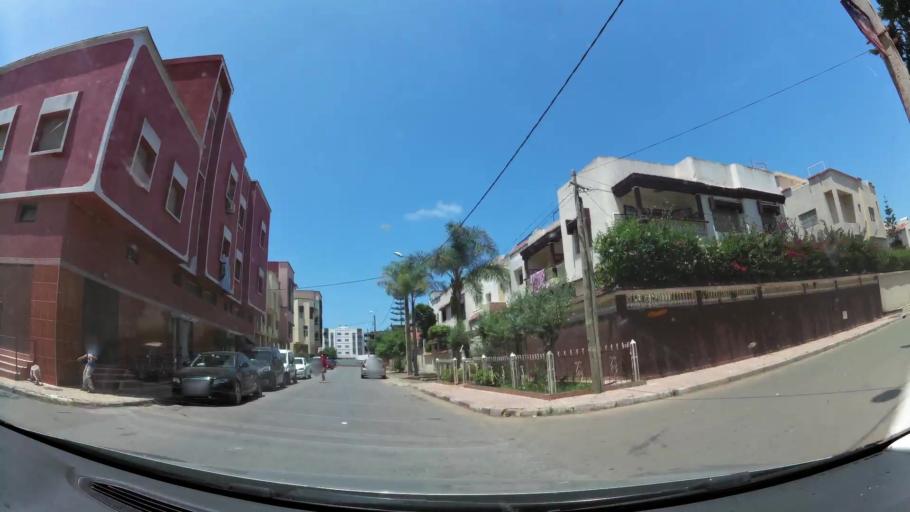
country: MA
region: Gharb-Chrarda-Beni Hssen
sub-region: Kenitra Province
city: Kenitra
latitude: 34.2635
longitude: -6.6221
